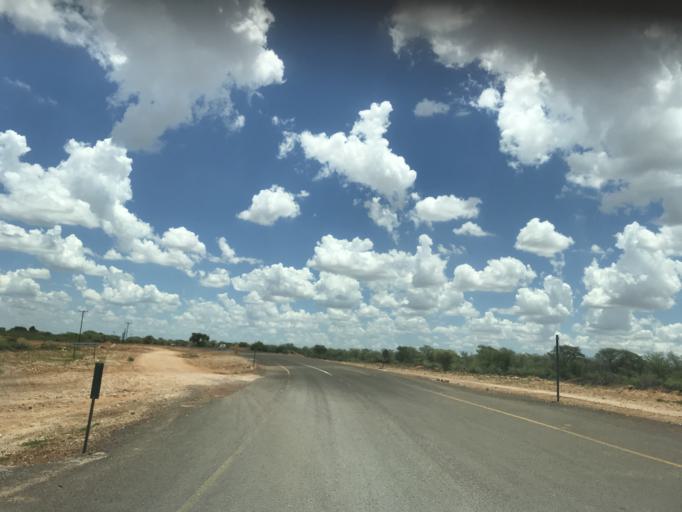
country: BW
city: Mabuli
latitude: -25.8015
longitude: 24.7090
